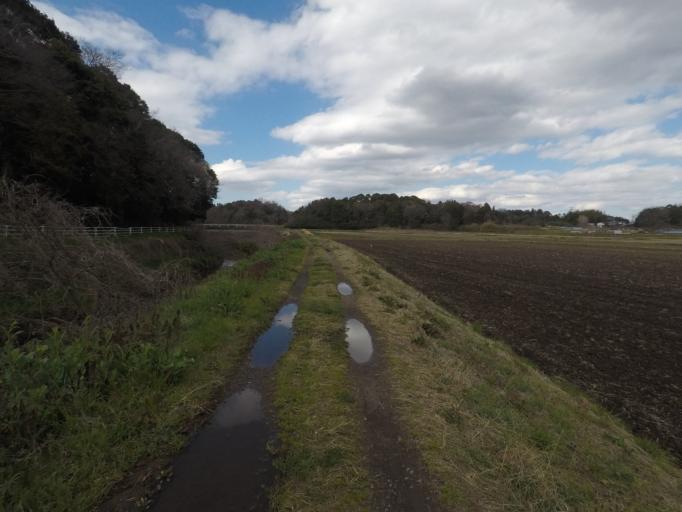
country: JP
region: Ibaraki
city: Ushiku
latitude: 35.9951
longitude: 140.1168
